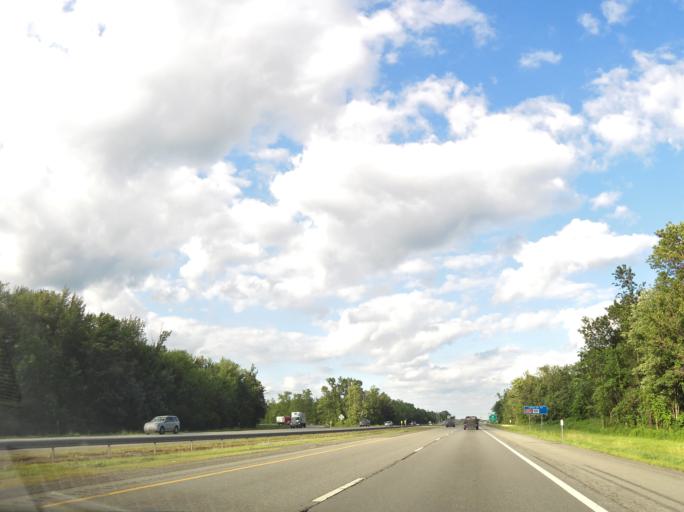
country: US
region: New York
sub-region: Erie County
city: Akron
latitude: 42.9981
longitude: -78.4218
